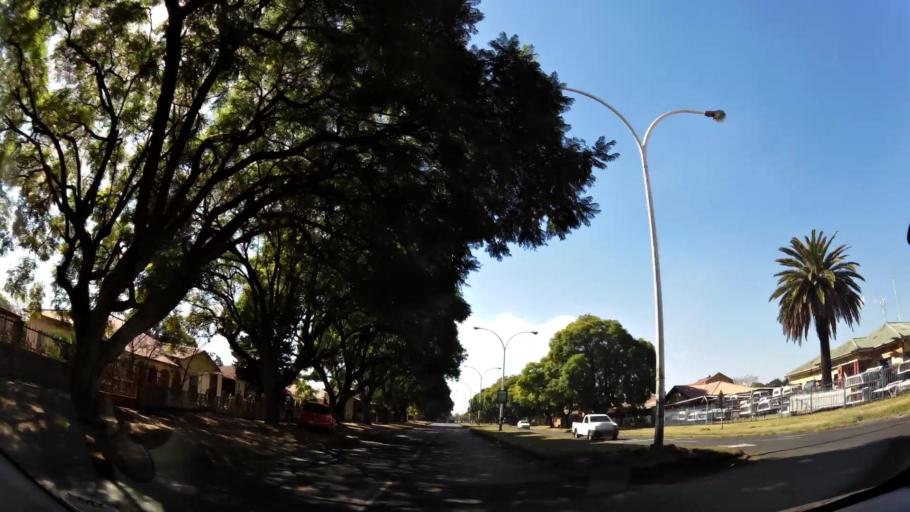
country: ZA
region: Mpumalanga
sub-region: Nkangala District Municipality
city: Witbank
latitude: -25.8677
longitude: 29.2163
